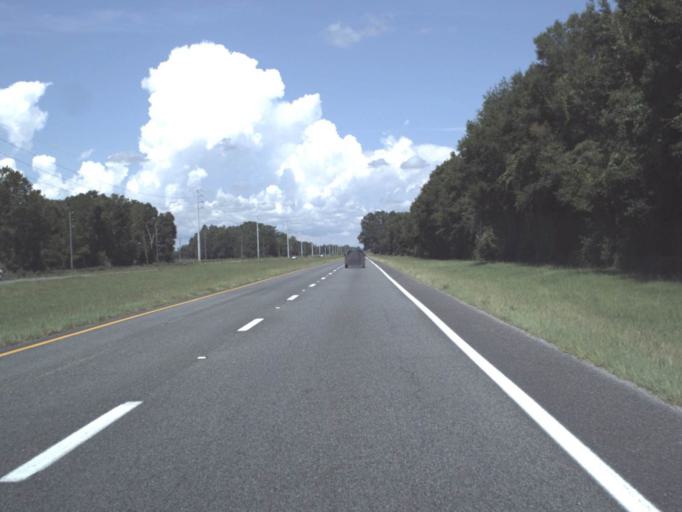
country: US
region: Florida
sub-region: Levy County
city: Chiefland
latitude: 29.4750
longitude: -82.8110
